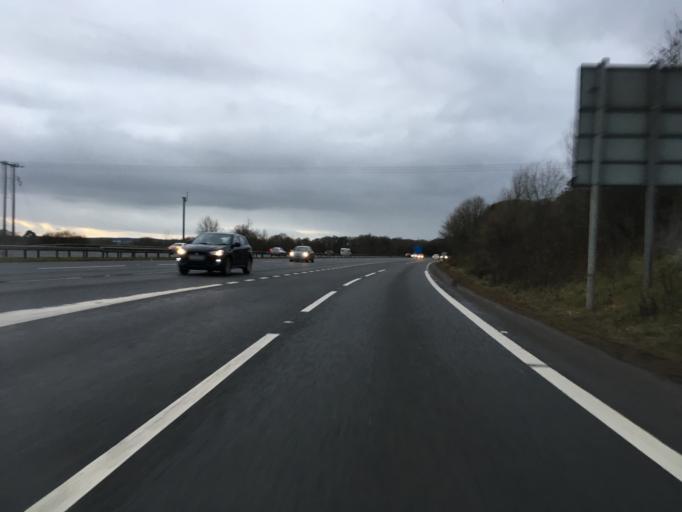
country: GB
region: Wales
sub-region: Cardiff
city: Pentyrch
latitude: 51.5061
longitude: -3.3166
